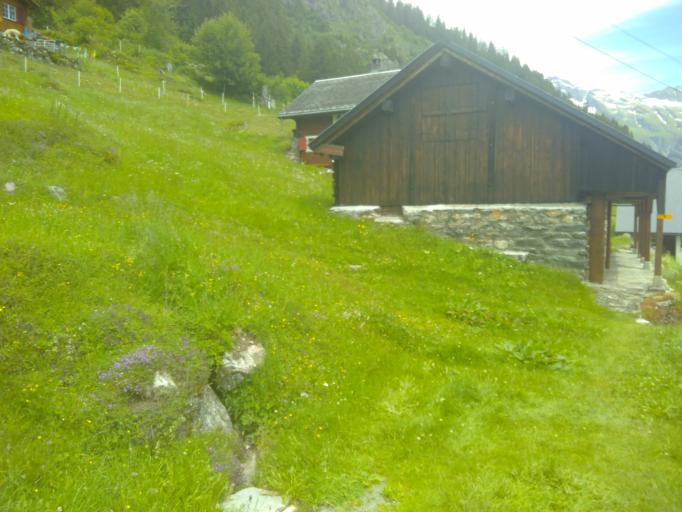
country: CH
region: Uri
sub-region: Uri
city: Silenen
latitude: 46.7773
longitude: 8.7253
